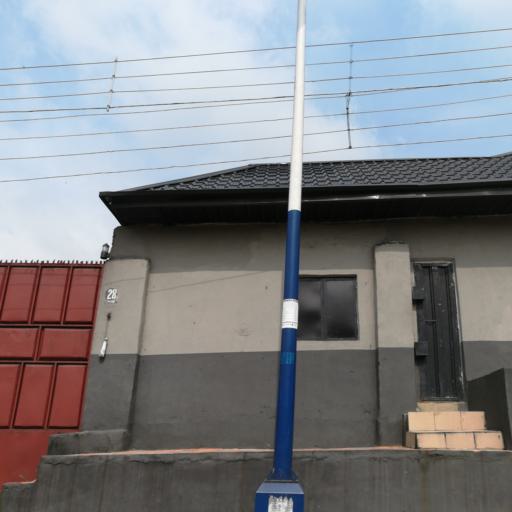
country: NG
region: Rivers
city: Port Harcourt
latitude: 4.8348
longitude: 7.0663
